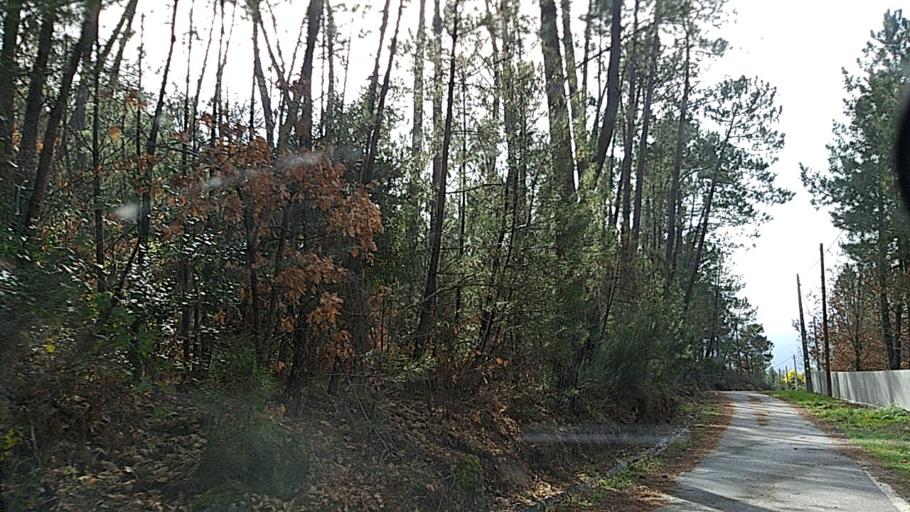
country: PT
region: Guarda
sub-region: Fornos de Algodres
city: Fornos de Algodres
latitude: 40.6350
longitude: -7.5382
